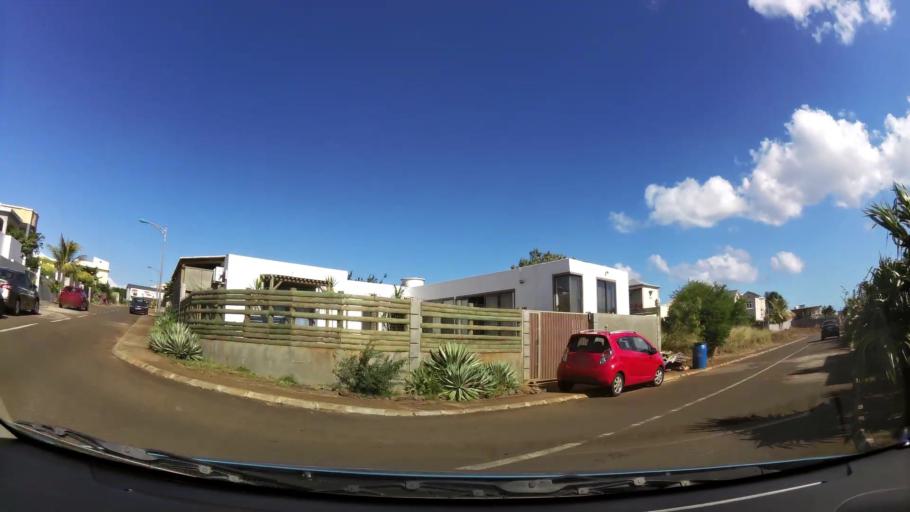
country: MU
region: Black River
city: Albion
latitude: -20.2165
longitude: 57.4150
